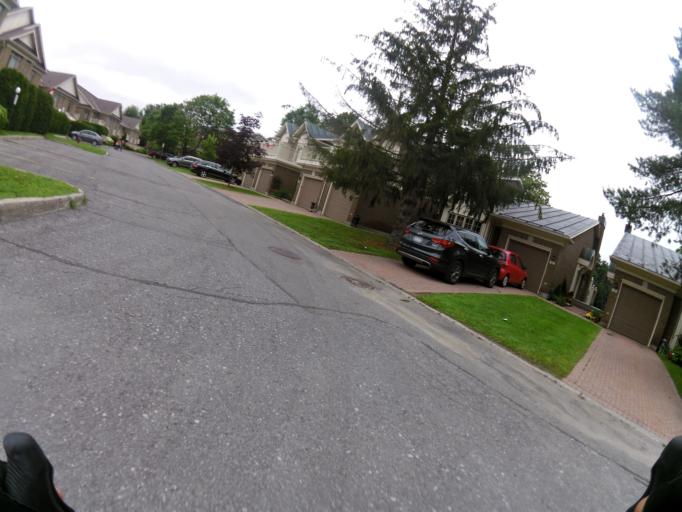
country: CA
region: Ontario
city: Ottawa
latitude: 45.3250
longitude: -75.7006
